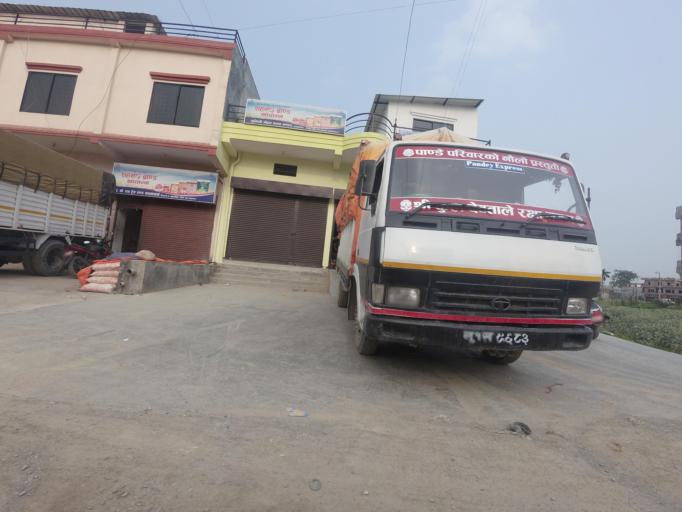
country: NP
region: Western Region
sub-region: Lumbini Zone
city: Bhairahawa
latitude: 27.5114
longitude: 83.4375
